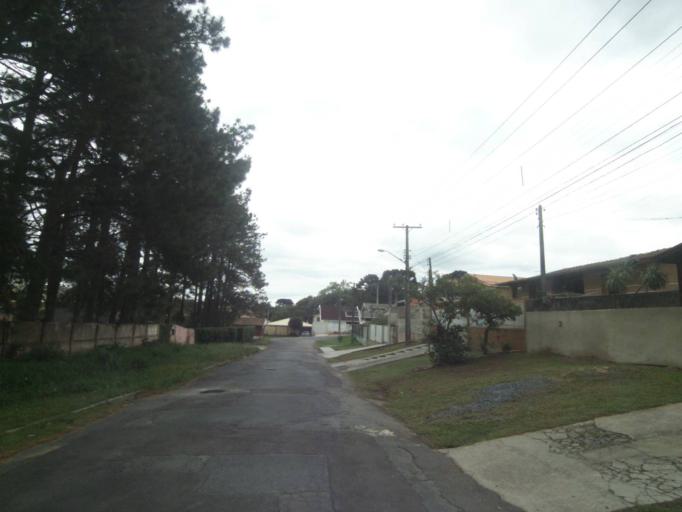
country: BR
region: Parana
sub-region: Curitiba
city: Curitiba
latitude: -25.3855
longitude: -49.2874
